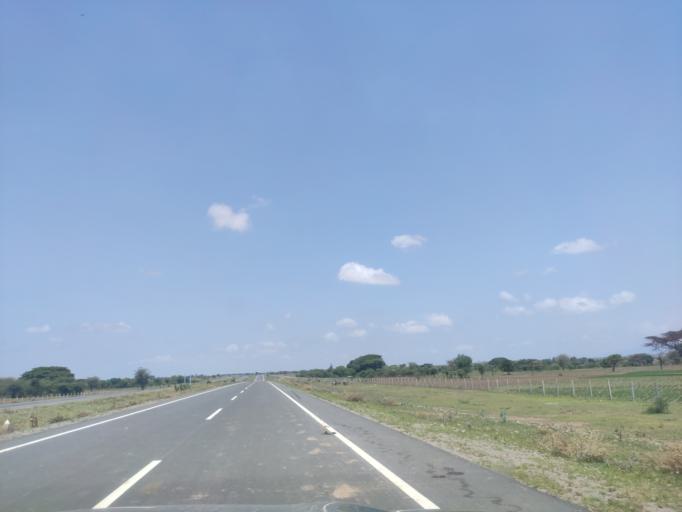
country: ET
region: Oromiya
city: Mojo
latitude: 8.2961
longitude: 38.9294
